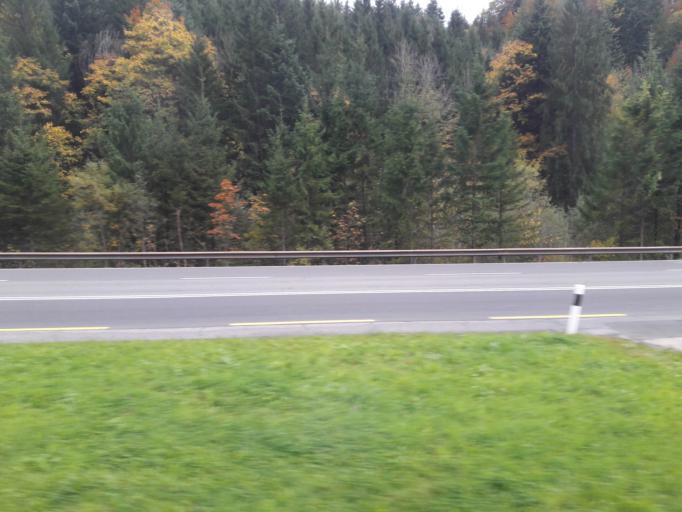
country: CH
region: Schwyz
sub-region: Bezirk Schwyz
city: Sattel
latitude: 47.0879
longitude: 8.6573
